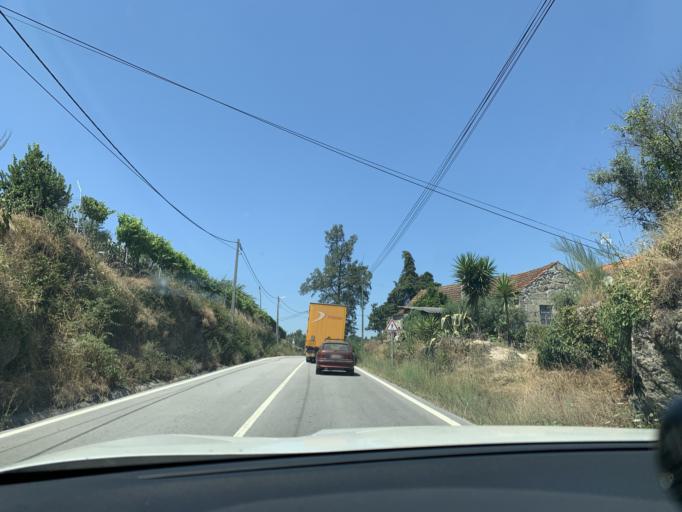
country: PT
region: Viseu
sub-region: Mangualde
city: Mangualde
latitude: 40.5915
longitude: -7.8006
